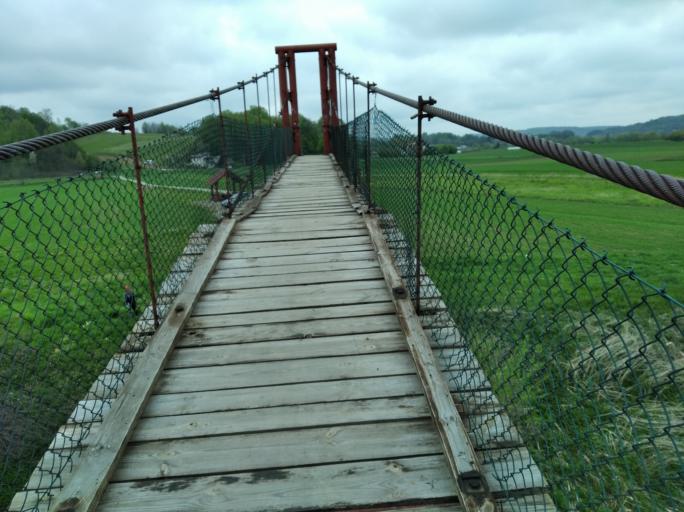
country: PL
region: Subcarpathian Voivodeship
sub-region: Powiat brzozowski
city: Nozdrzec
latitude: 49.7483
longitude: 22.2233
